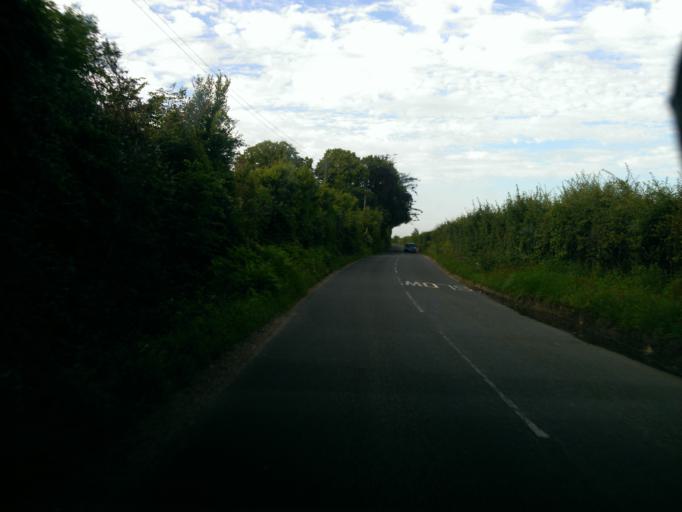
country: GB
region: England
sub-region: Essex
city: Great Bentley
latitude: 51.8589
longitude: 1.0643
